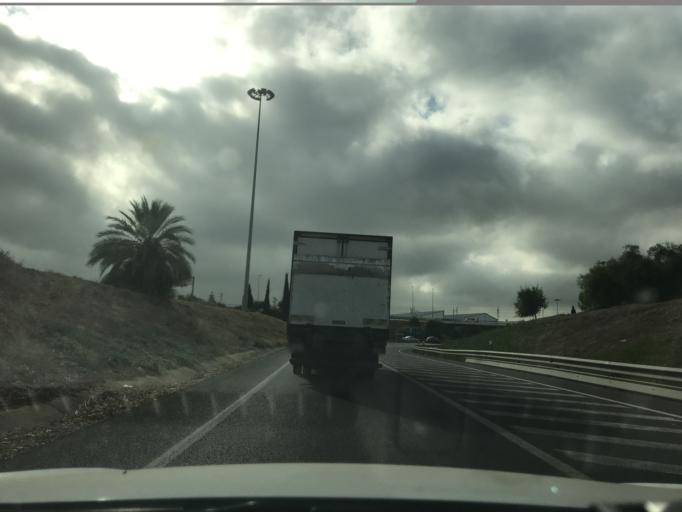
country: ES
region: Andalusia
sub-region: Provincia de Sevilla
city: San Juan de Aznalfarache
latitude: 37.3706
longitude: -6.0152
